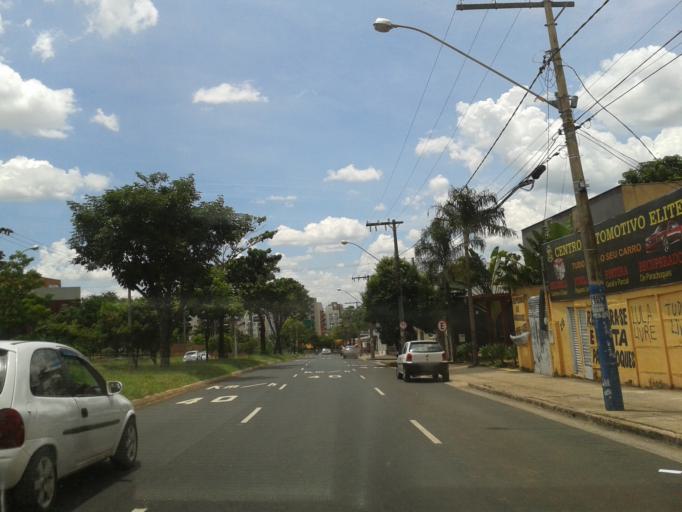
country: BR
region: Minas Gerais
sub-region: Uberlandia
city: Uberlandia
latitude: -18.9163
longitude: -48.2567
